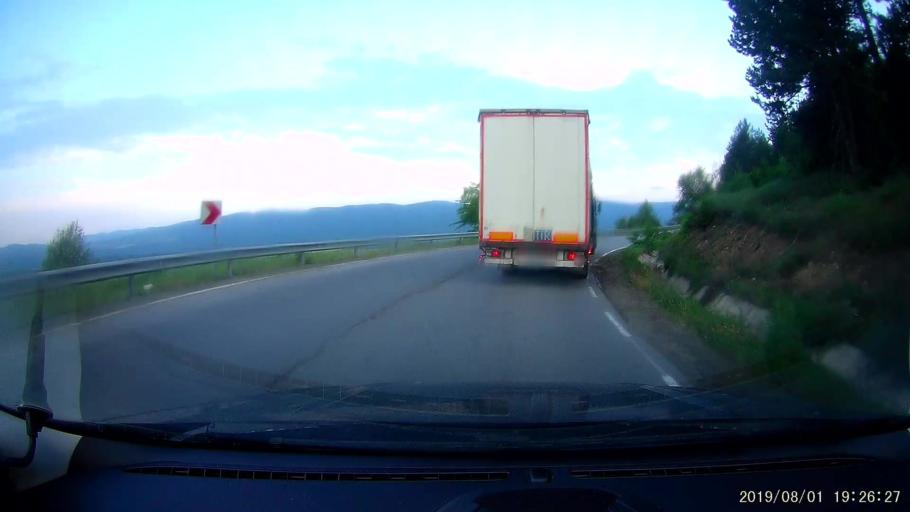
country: BG
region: Burgas
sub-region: Obshtina Sungurlare
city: Sungurlare
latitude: 42.8574
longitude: 26.9403
